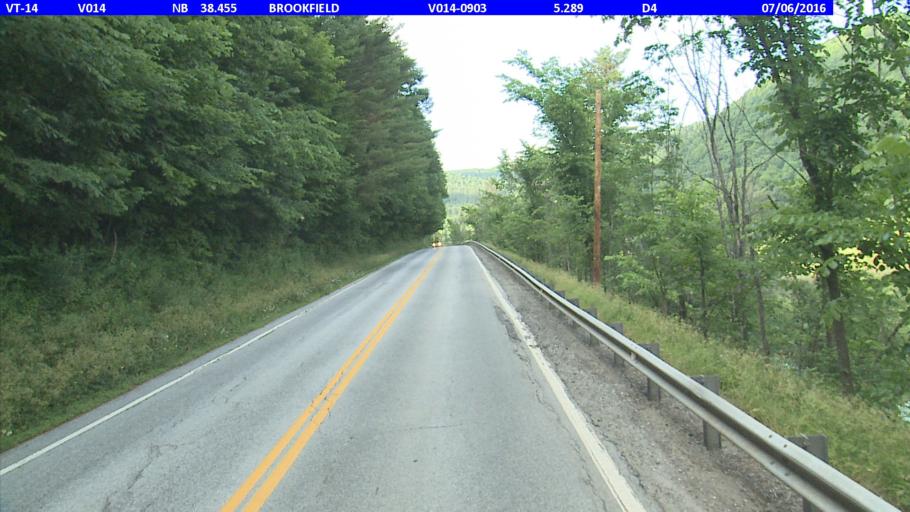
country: US
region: Vermont
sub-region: Orange County
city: Williamstown
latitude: 44.0526
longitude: -72.5635
